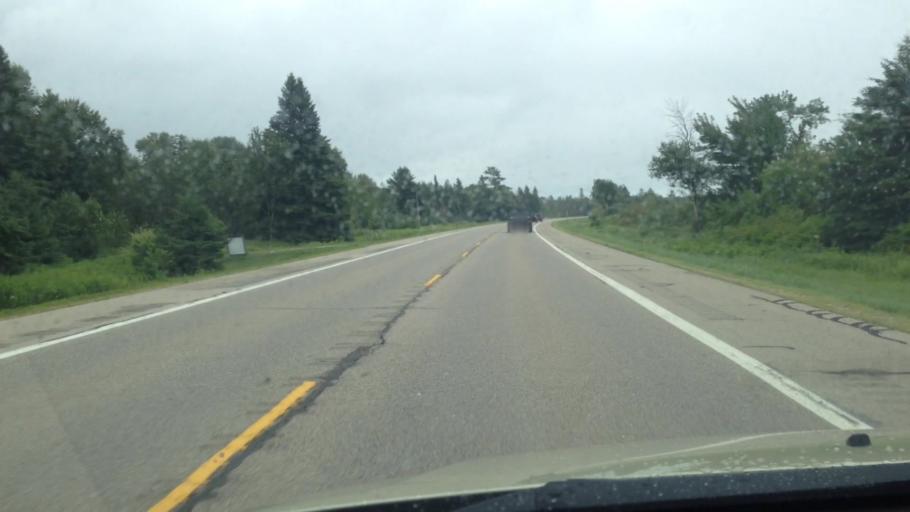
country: US
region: Michigan
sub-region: Schoolcraft County
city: Manistique
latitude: 45.9000
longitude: -86.5612
